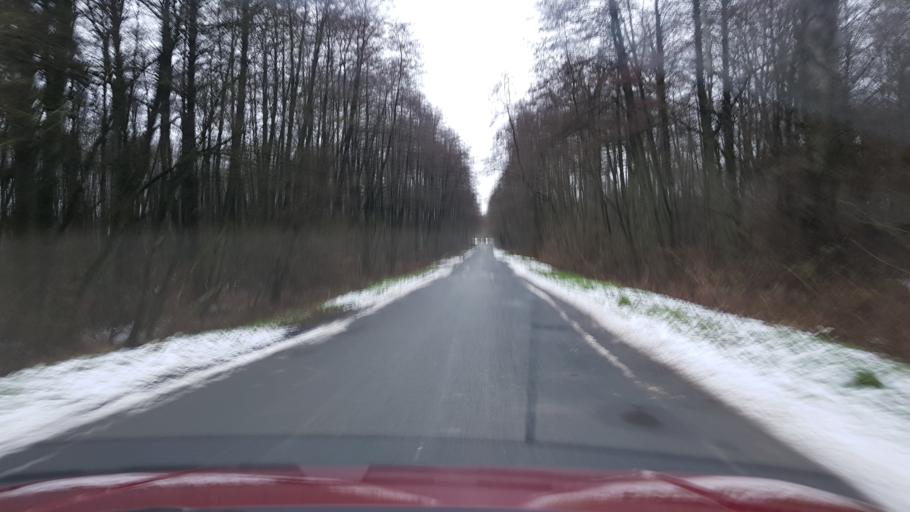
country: PL
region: West Pomeranian Voivodeship
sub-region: Powiat goleniowski
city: Nowogard
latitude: 53.6799
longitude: 15.2286
